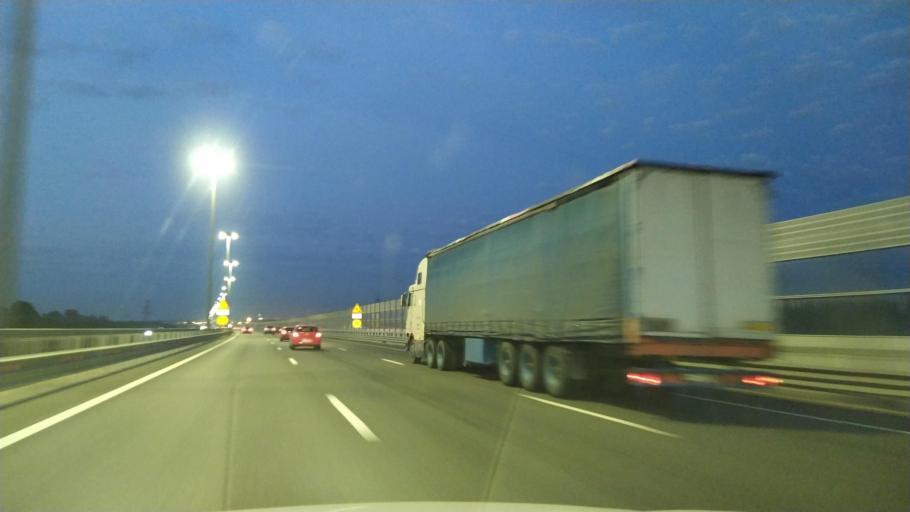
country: RU
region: Leningrad
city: Parnas
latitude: 60.0955
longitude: 30.3198
